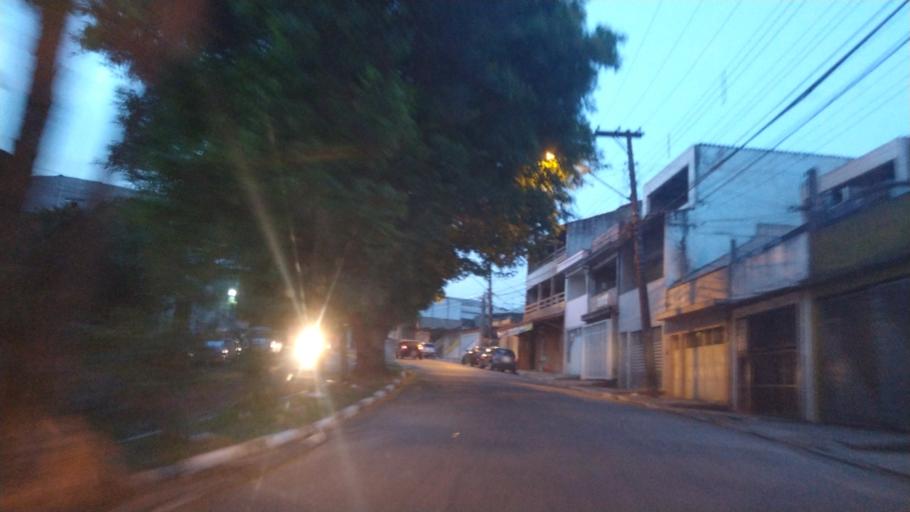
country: BR
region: Sao Paulo
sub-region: Aruja
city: Aruja
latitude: -23.4154
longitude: -46.4042
